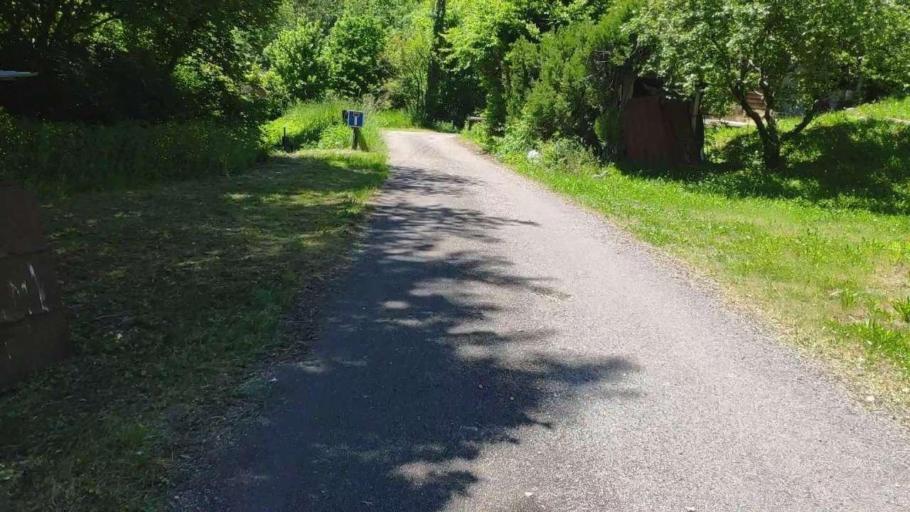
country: FR
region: Franche-Comte
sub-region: Departement du Jura
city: Perrigny
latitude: 46.7384
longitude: 5.6294
